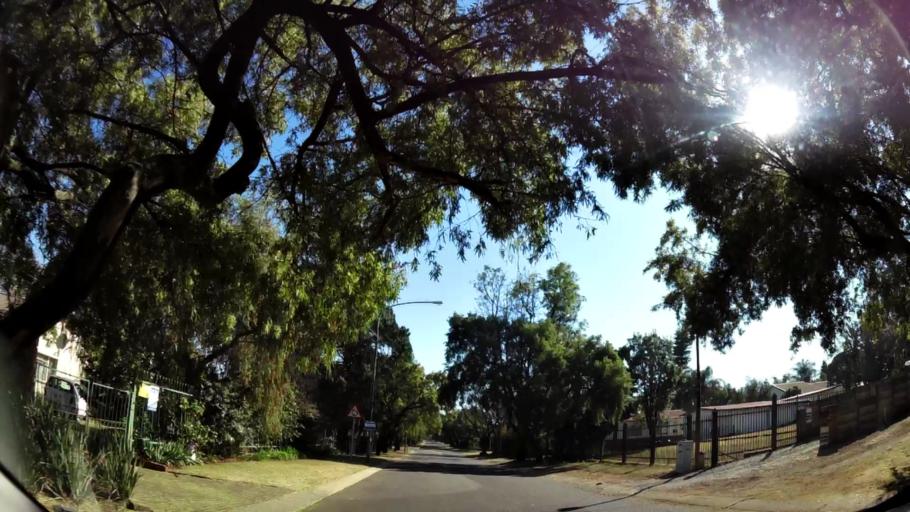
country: ZA
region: Gauteng
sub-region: City of Tshwane Metropolitan Municipality
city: Centurion
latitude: -25.8306
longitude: 28.2147
